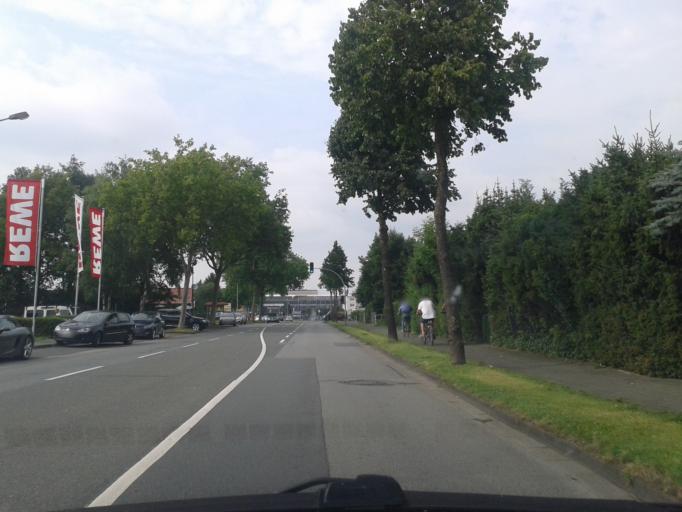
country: DE
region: North Rhine-Westphalia
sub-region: Regierungsbezirk Detmold
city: Paderborn
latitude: 51.7456
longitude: 8.7580
